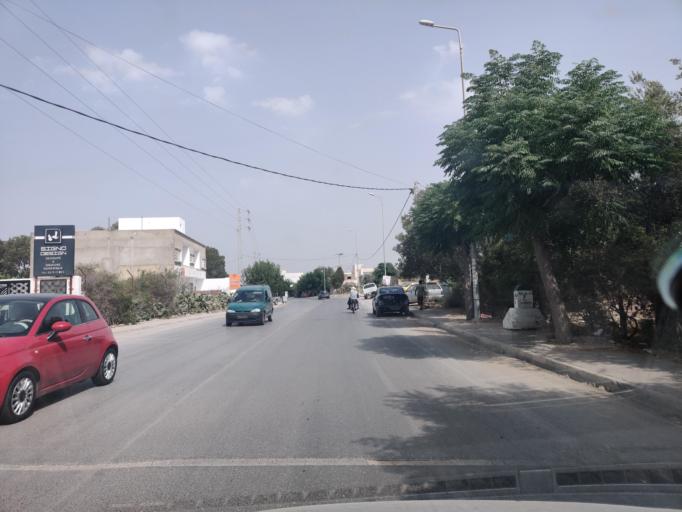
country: TN
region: Nabul
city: Al Hammamat
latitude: 36.4138
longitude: 10.5970
